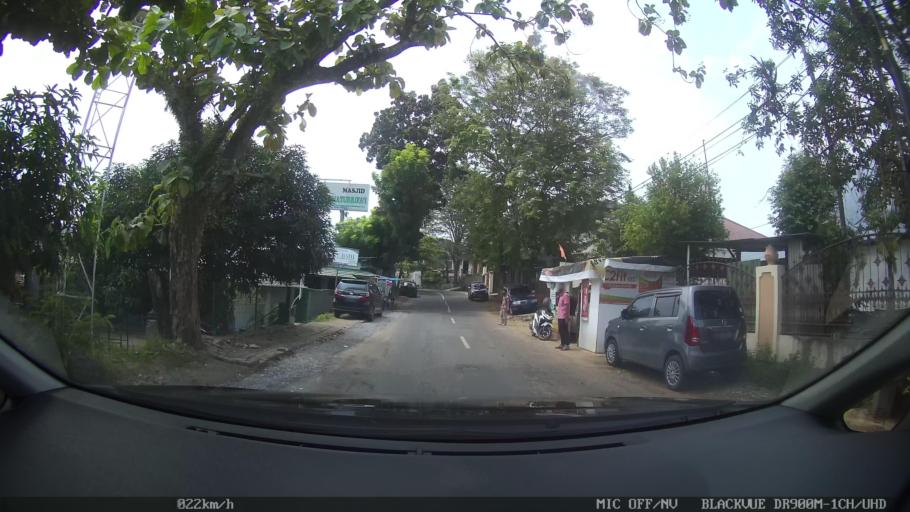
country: ID
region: Lampung
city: Bandarlampung
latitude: -5.4322
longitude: 105.2644
